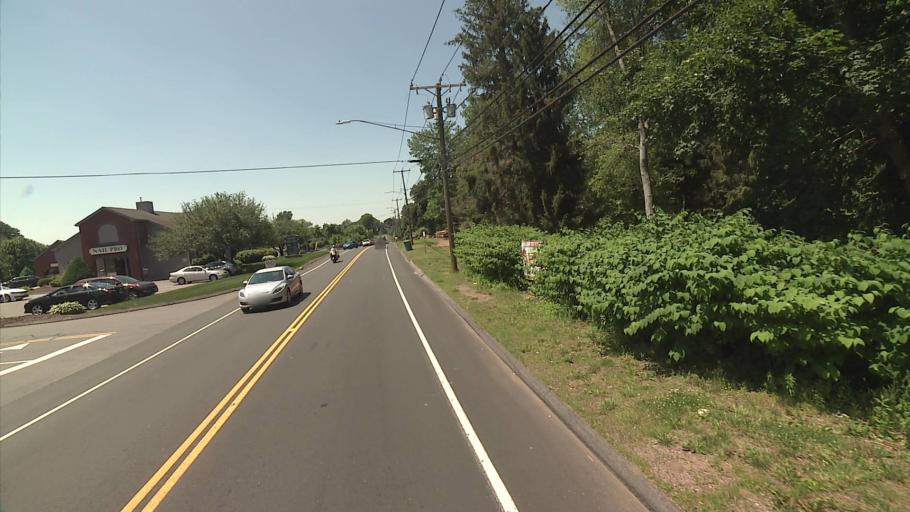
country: US
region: Connecticut
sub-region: Hartford County
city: Manchester
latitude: 41.8208
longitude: -72.5422
